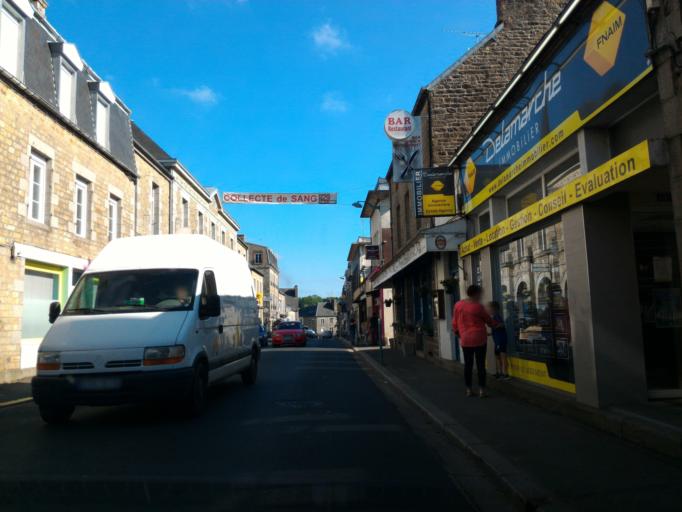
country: FR
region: Lower Normandy
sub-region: Departement de la Manche
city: La Haye-Pesnel
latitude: 48.7961
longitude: -1.3979
